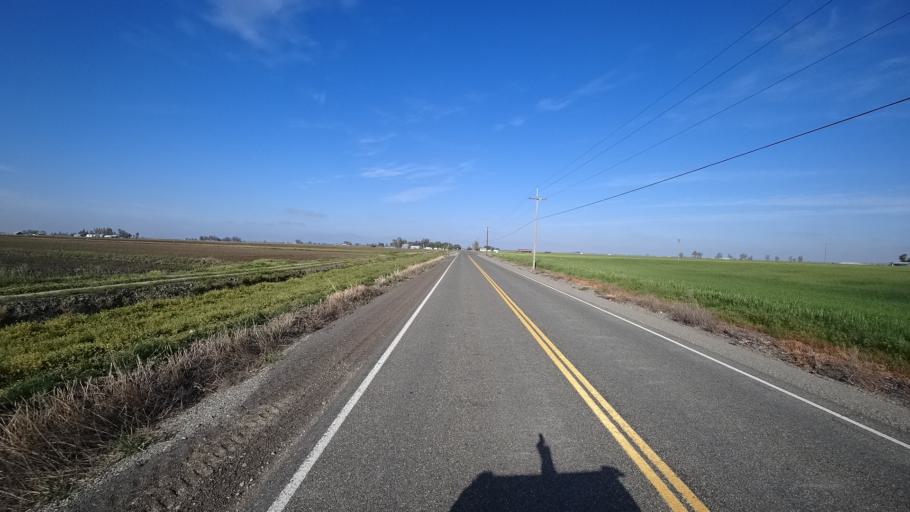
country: US
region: California
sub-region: Glenn County
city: Willows
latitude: 39.5828
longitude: -122.0869
